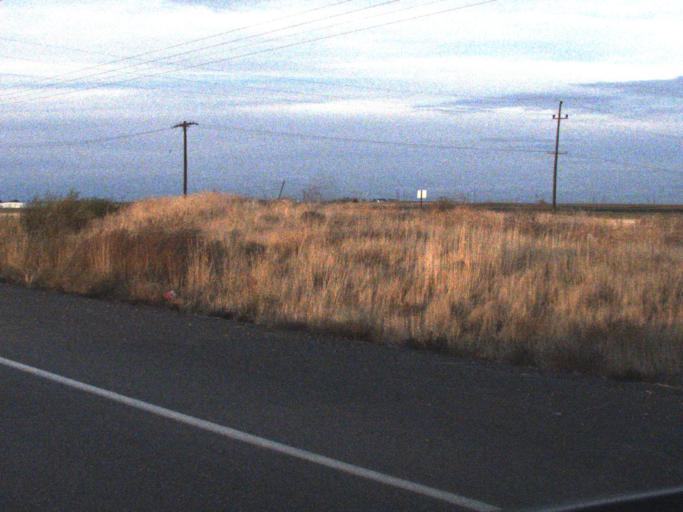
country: US
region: Washington
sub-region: Walla Walla County
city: Burbank
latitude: 46.2204
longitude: -119.0290
